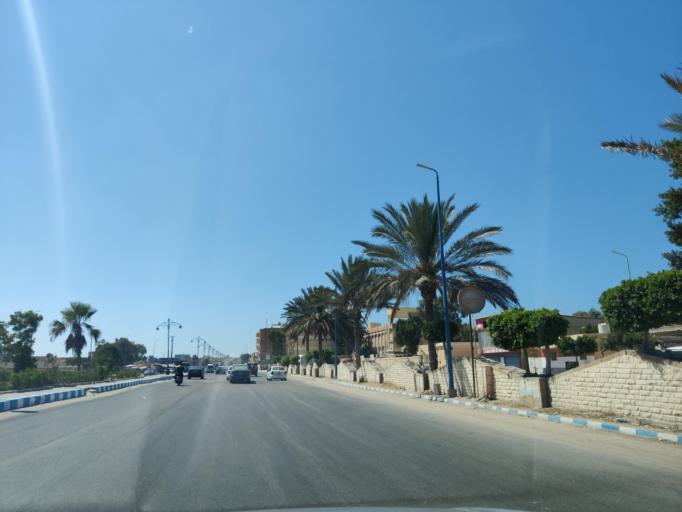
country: EG
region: Muhafazat Matruh
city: Mersa Matruh
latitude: 31.3399
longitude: 27.2494
